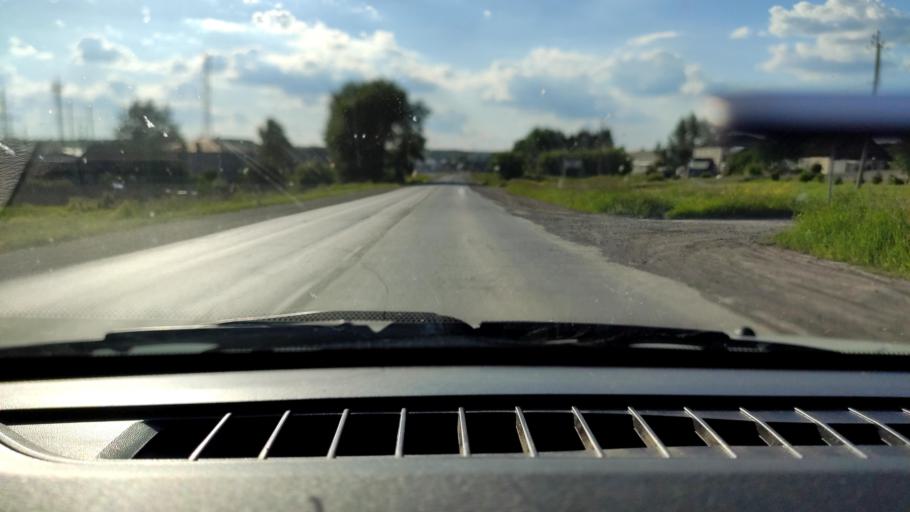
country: RU
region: Perm
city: Orda
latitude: 57.1892
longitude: 56.9101
